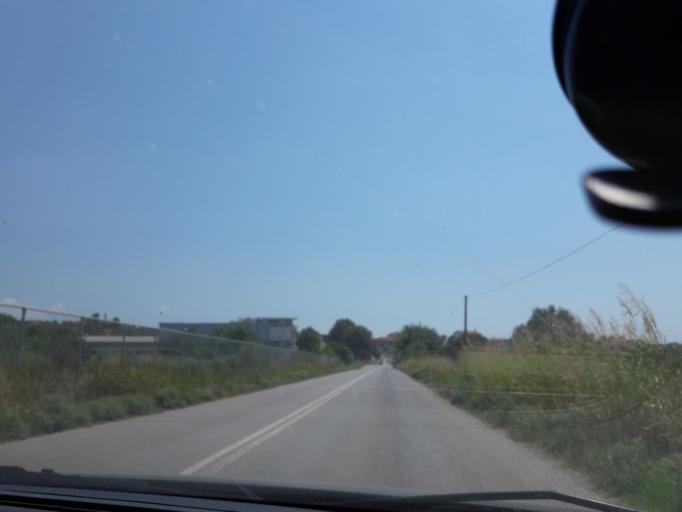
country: GR
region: Central Macedonia
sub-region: Nomos Chalkidikis
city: Nea Kallikrateia
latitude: 40.3266
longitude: 23.0634
